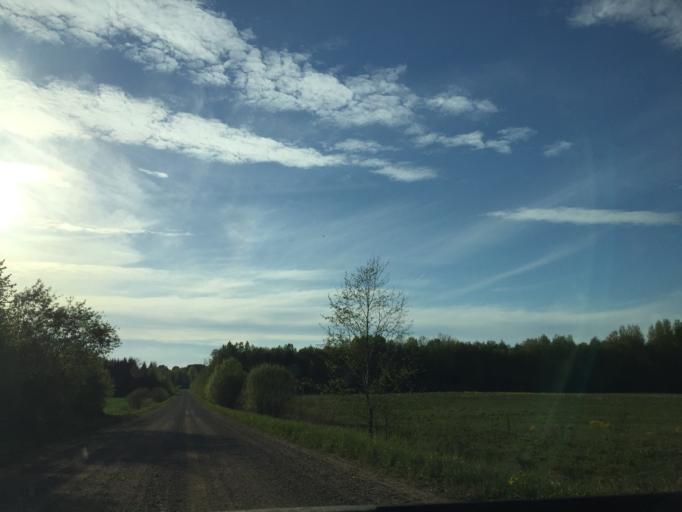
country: LV
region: Limbazu Rajons
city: Limbazi
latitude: 57.3976
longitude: 24.5612
